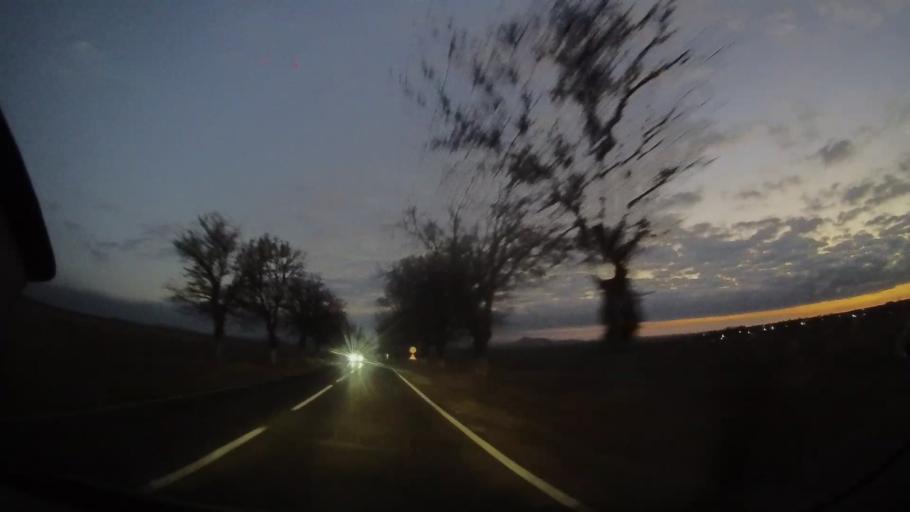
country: RO
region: Tulcea
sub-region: Comuna Frecatei
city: Cataloi
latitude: 45.0938
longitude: 28.7415
